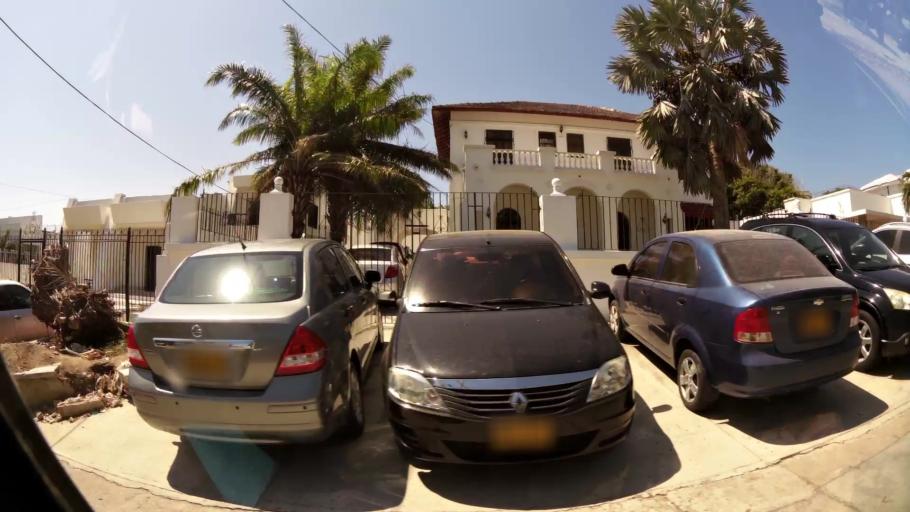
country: CO
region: Atlantico
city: Barranquilla
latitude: 10.9972
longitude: -74.7942
